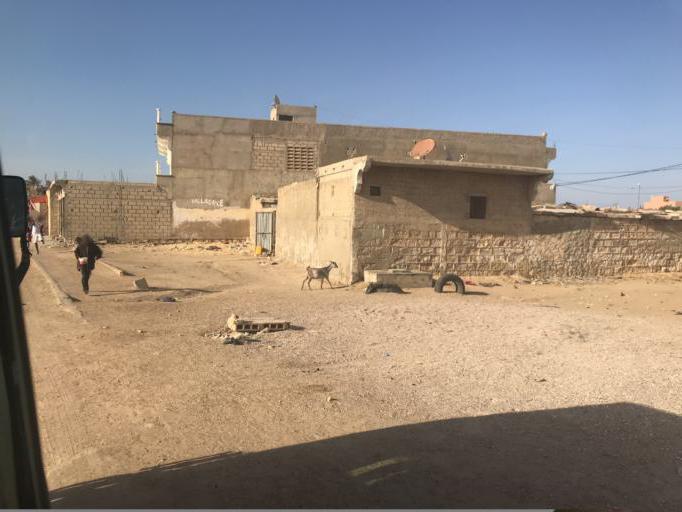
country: SN
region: Saint-Louis
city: Saint-Louis
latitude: 15.9970
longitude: -16.4942
